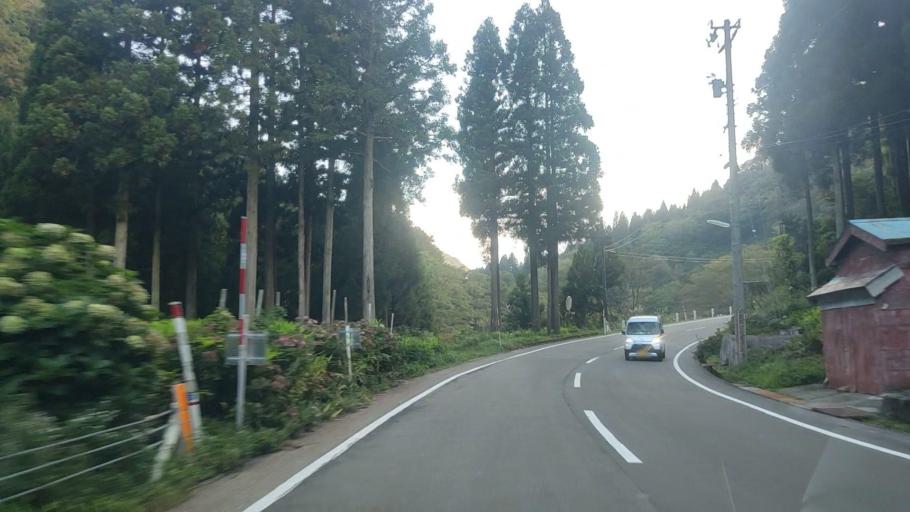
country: JP
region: Toyama
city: Yatsuomachi-higashikumisaka
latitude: 36.4944
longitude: 137.0493
